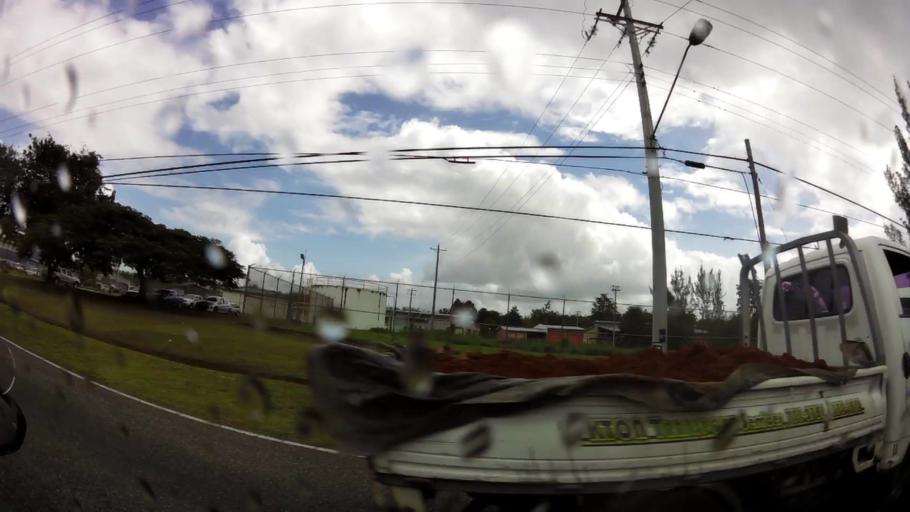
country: TT
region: Tunapuna/Piarco
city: Arouca
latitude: 10.6192
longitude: -61.3422
